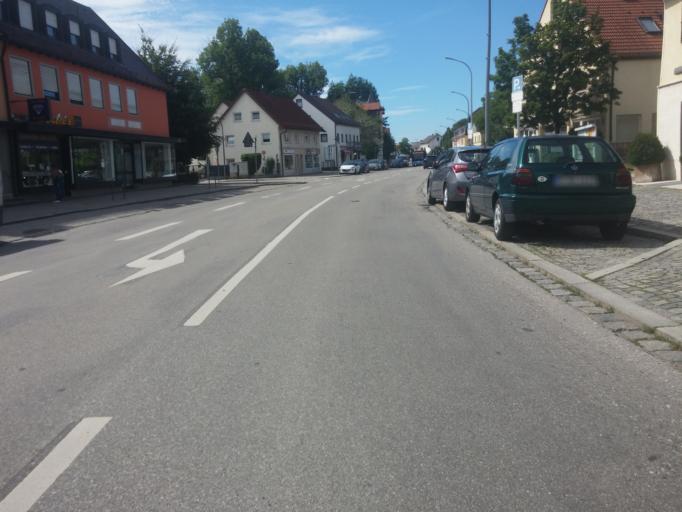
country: DE
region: Bavaria
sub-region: Upper Bavaria
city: Neubiberg
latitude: 48.1225
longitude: 11.6691
